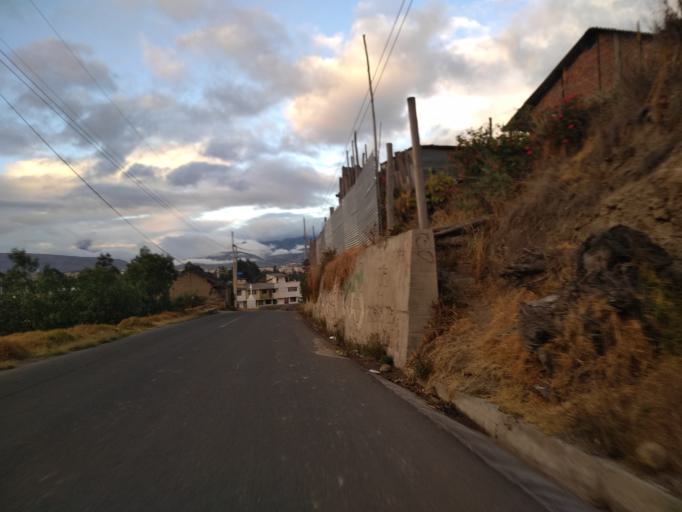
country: EC
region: Chimborazo
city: Riobamba
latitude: -1.6852
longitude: -78.6801
